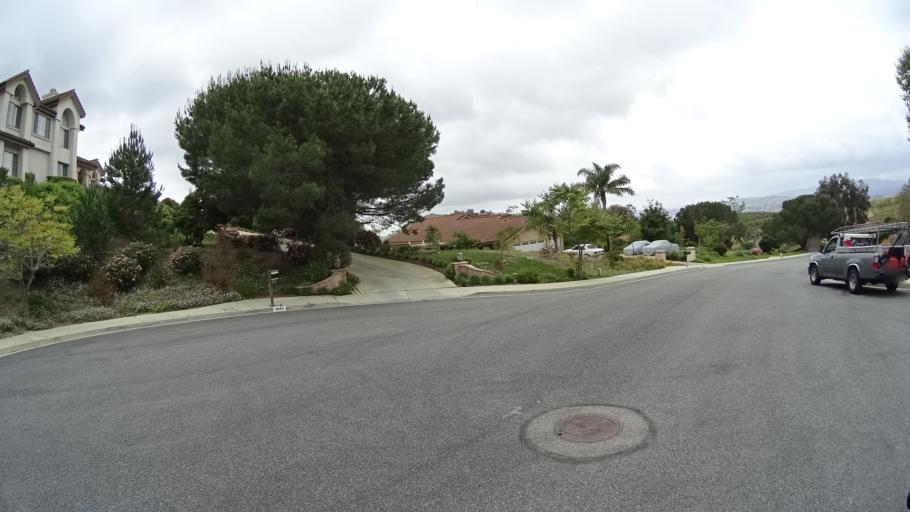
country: US
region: California
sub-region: Ventura County
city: Moorpark
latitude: 34.2280
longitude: -118.8909
